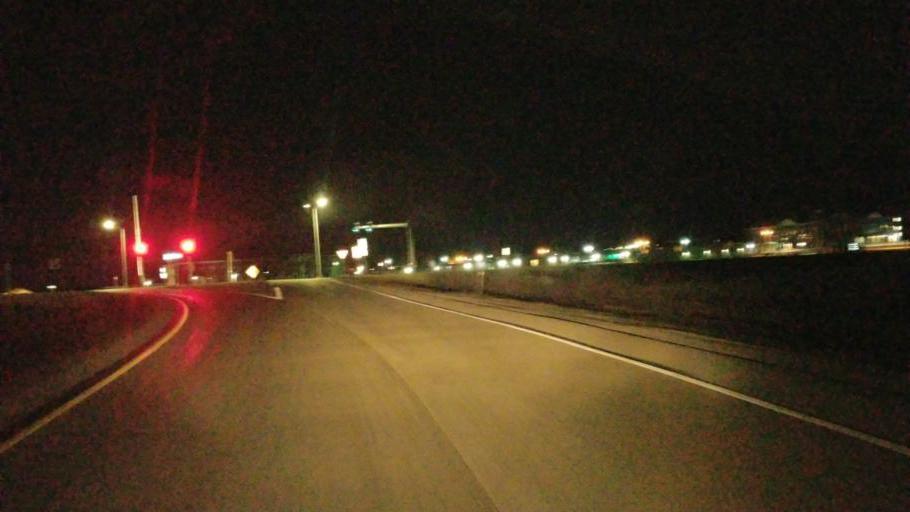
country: US
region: Wisconsin
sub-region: Fond du Lac County
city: Fond du Lac
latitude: 43.7588
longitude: -88.4764
